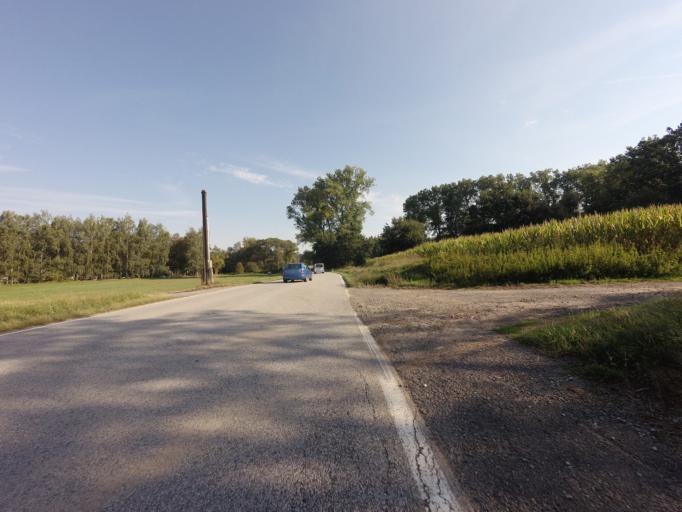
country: CZ
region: Jihocesky
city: Tyn nad Vltavou
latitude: 49.2459
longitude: 14.4198
